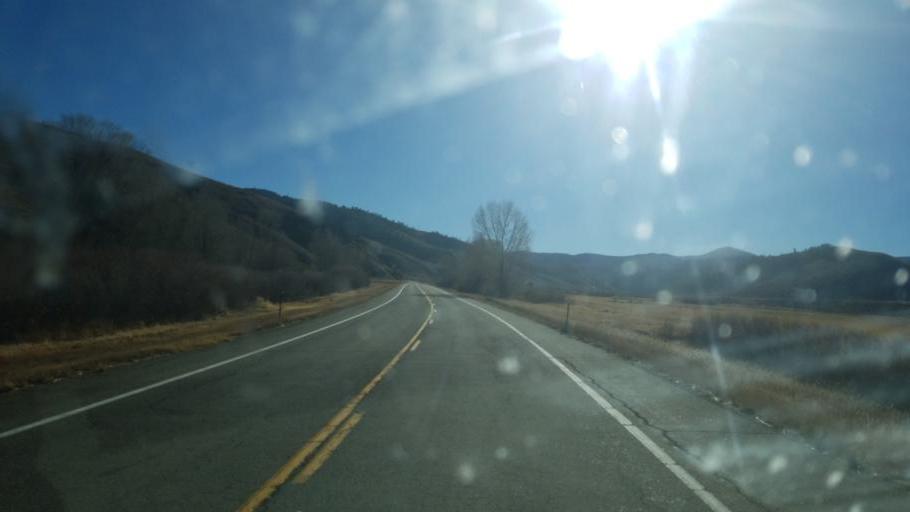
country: US
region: Colorado
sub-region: Gunnison County
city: Gunnison
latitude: 38.4177
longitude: -106.5198
